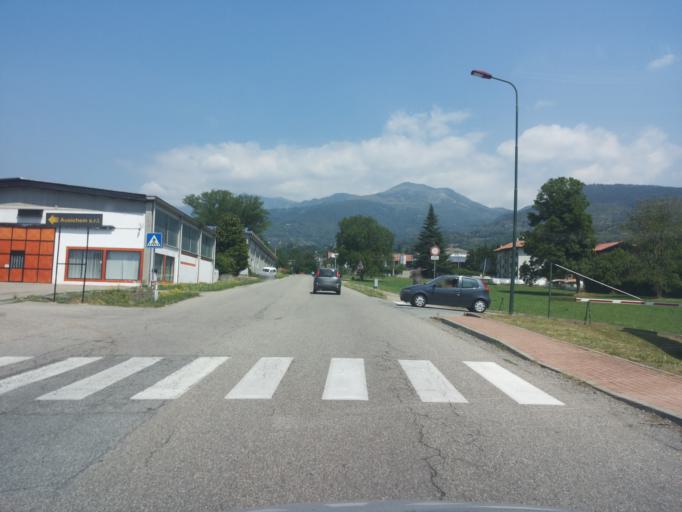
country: IT
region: Piedmont
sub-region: Provincia di Biella
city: Andorno Cacciorna
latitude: 45.6049
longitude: 8.0543
